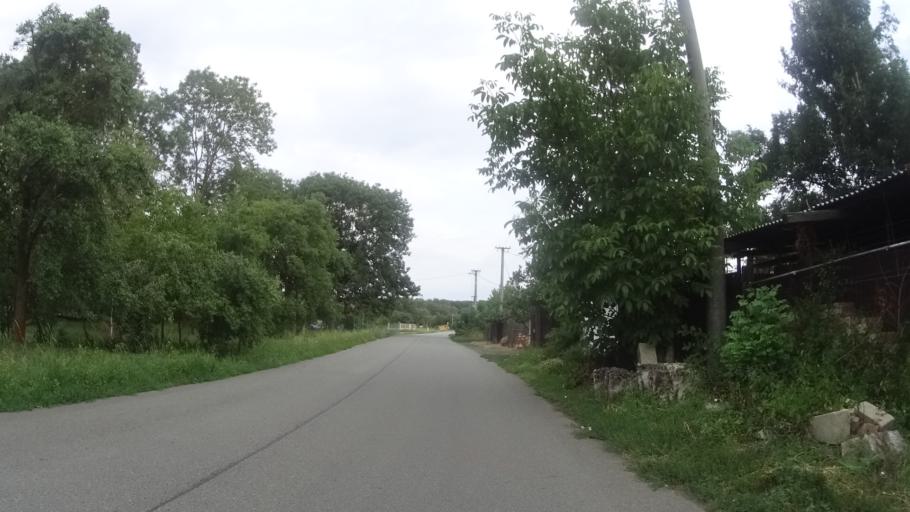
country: CZ
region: Zlin
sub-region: Okres Kromeriz
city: Kromeriz
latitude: 49.3140
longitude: 17.3905
